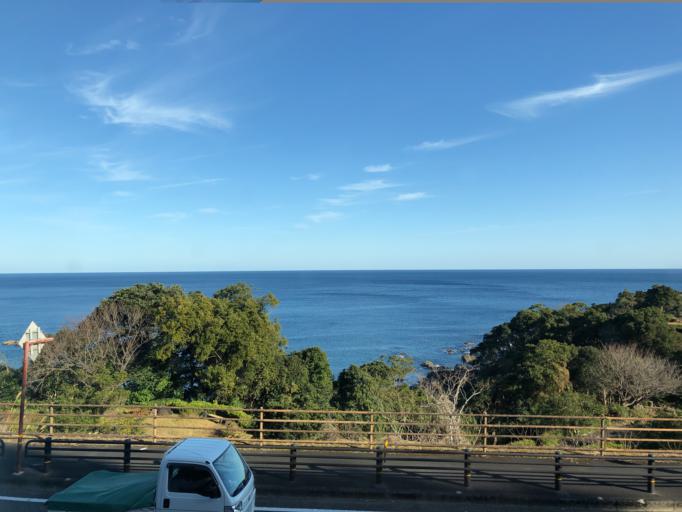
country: JP
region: Kochi
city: Nakamura
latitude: 33.0648
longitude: 133.1067
